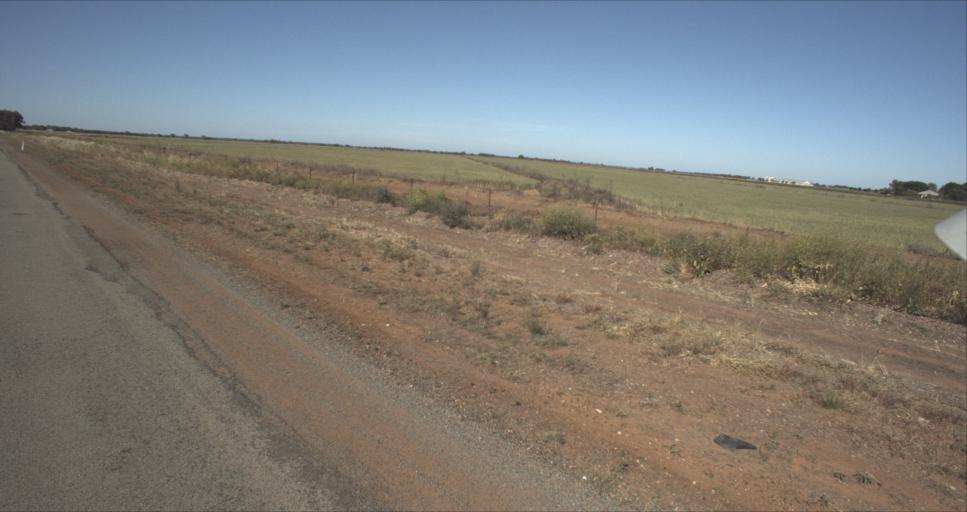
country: AU
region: New South Wales
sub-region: Leeton
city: Leeton
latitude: -34.5519
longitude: 146.3144
